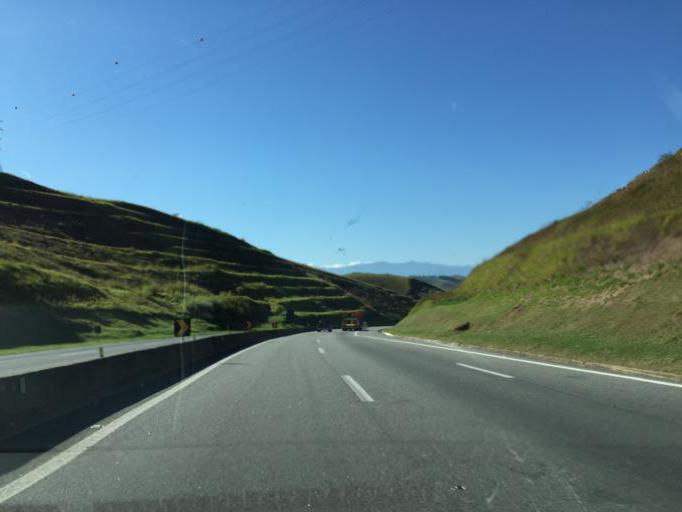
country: BR
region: Sao Paulo
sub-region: Cruzeiro
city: Cruzeiro
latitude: -22.6371
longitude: -44.9365
